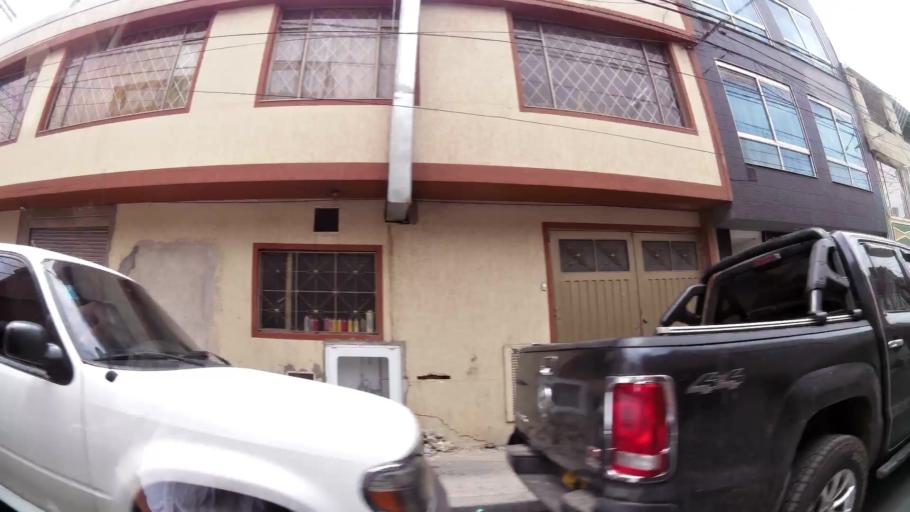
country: CO
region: Cundinamarca
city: La Calera
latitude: 4.7640
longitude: -74.0301
